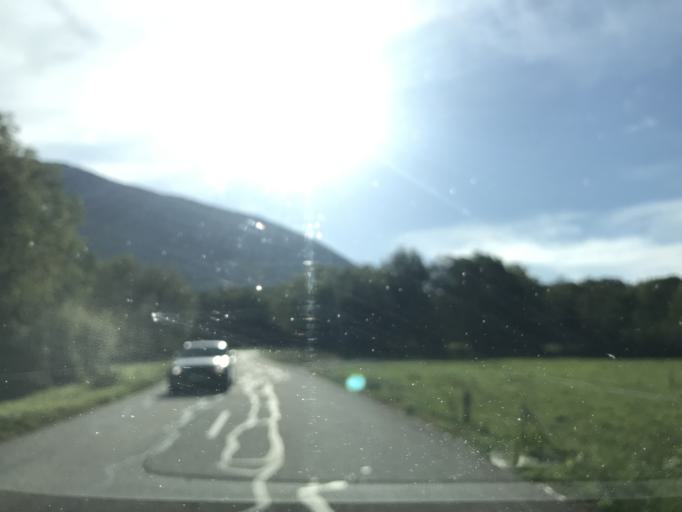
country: FR
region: Rhone-Alpes
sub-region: Departement de la Savoie
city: Yenne
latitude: 45.6673
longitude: 5.7883
